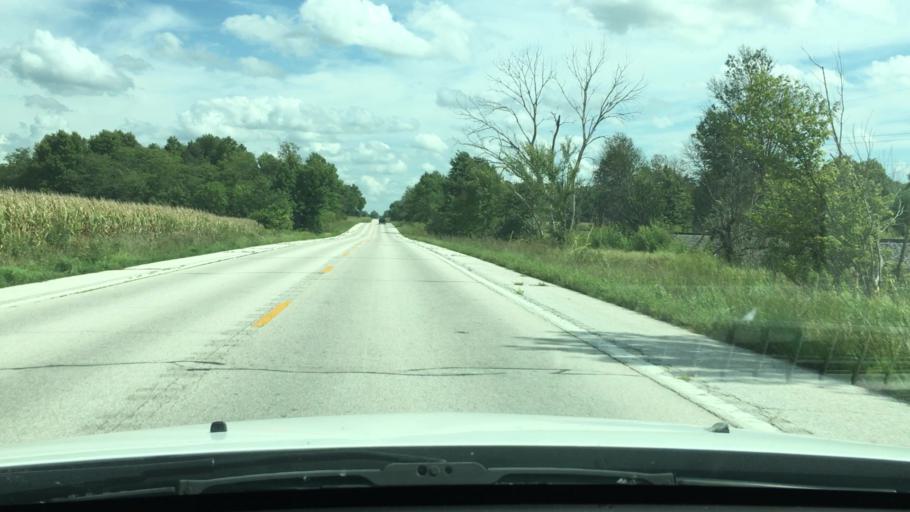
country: US
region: Missouri
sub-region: Audrain County
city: Vandalia
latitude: 39.3249
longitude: -91.4516
